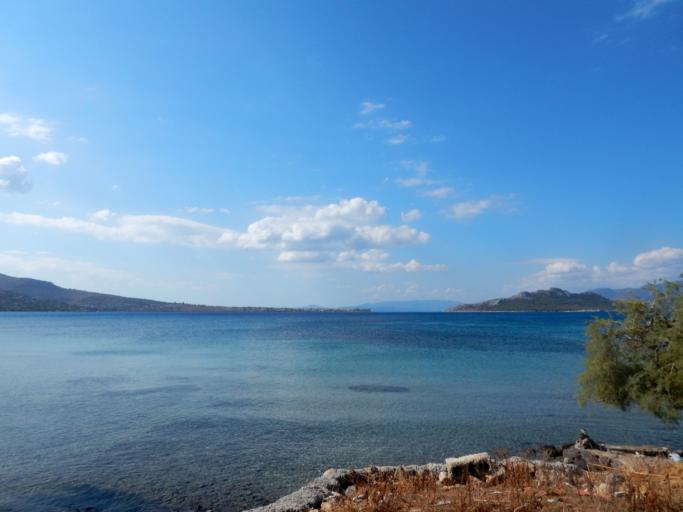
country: GR
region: Attica
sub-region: Nomos Piraios
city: Aegina
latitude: 37.7252
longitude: 23.4467
